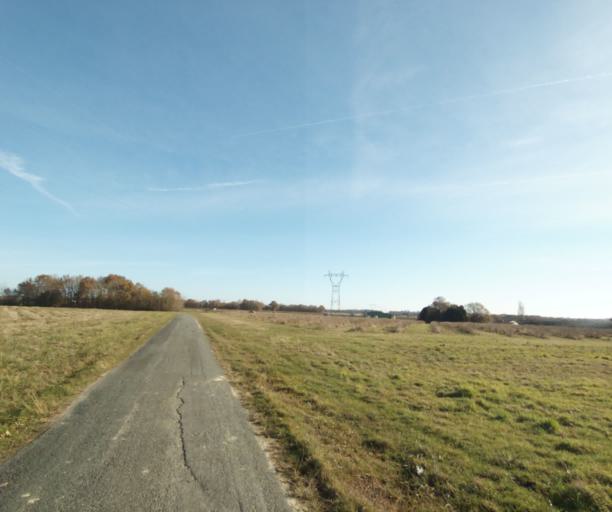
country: FR
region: Poitou-Charentes
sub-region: Departement de la Charente-Maritime
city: Cherac
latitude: 45.7442
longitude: -0.4842
